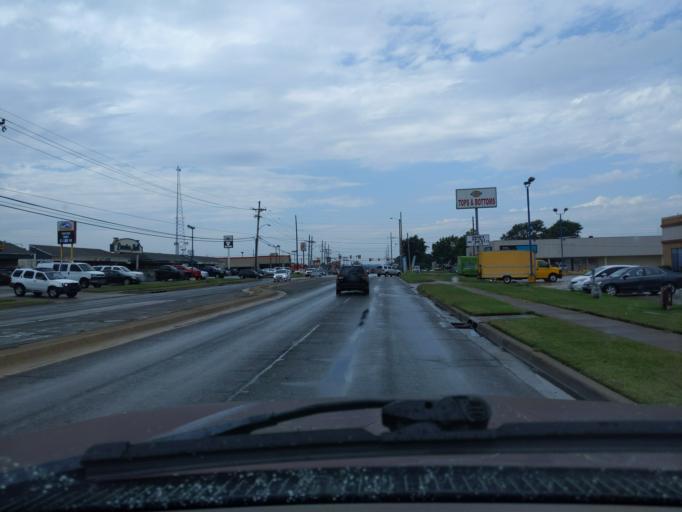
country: US
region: Oklahoma
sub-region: Tulsa County
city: Broken Arrow
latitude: 36.1336
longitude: -95.8485
